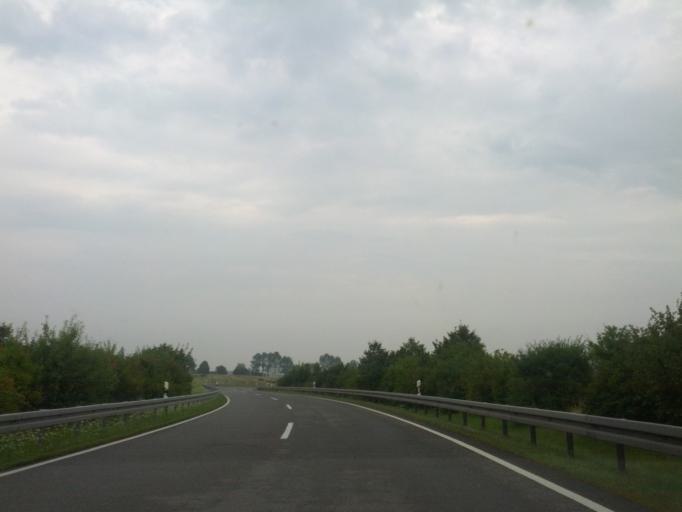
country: DE
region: Mecklenburg-Vorpommern
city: Ziesendorf
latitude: 54.0170
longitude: 12.0664
